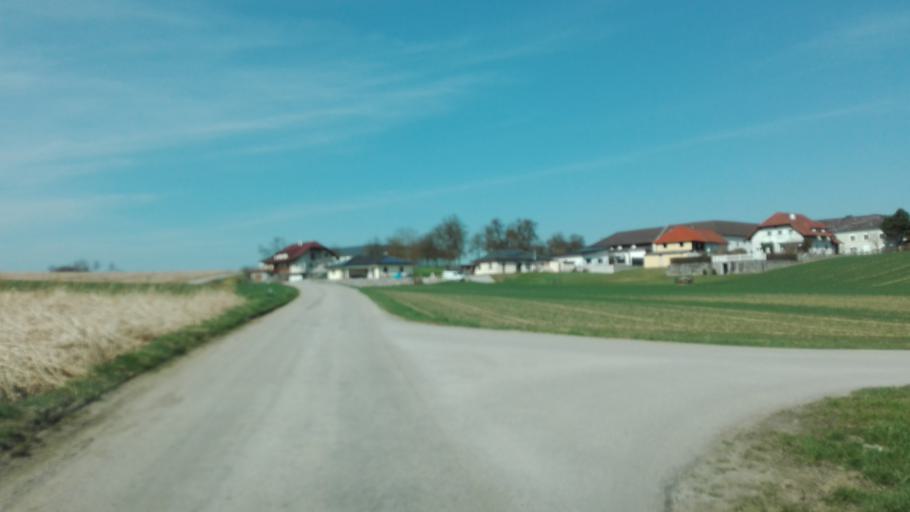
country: AT
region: Lower Austria
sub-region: Politischer Bezirk Amstetten
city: Ennsdorf
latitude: 48.2678
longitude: 14.5090
